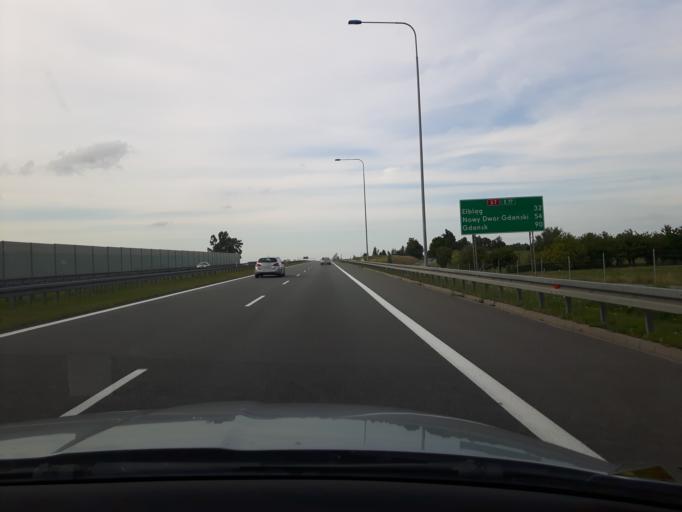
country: PL
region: Warmian-Masurian Voivodeship
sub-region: Powiat ostrodzki
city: Maldyty
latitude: 53.9766
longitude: 19.6971
